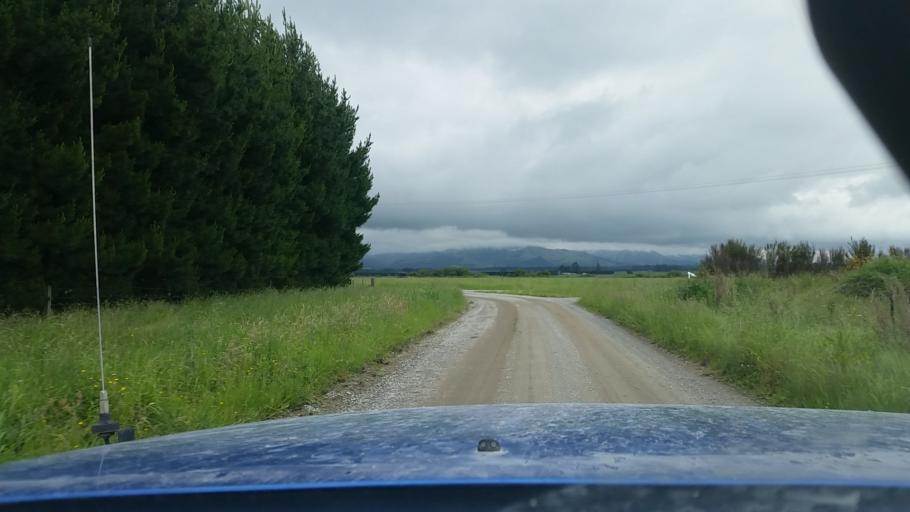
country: NZ
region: Canterbury
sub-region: Ashburton District
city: Methven
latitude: -43.6973
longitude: 171.4616
